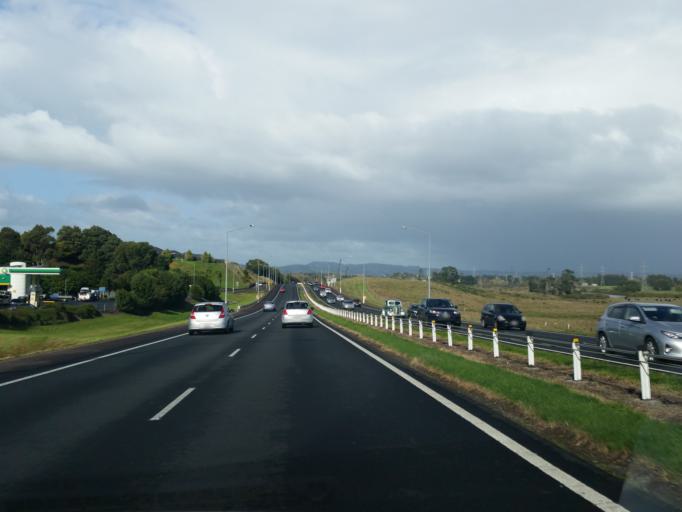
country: NZ
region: Auckland
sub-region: Auckland
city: Papakura
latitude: -37.0874
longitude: 174.9383
